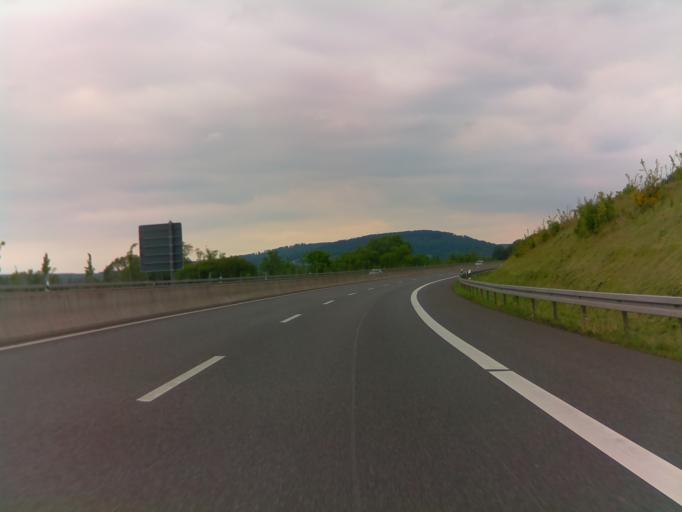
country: DE
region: Hesse
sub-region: Regierungsbezirk Giessen
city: Fronhausen
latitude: 50.7297
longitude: 8.7352
